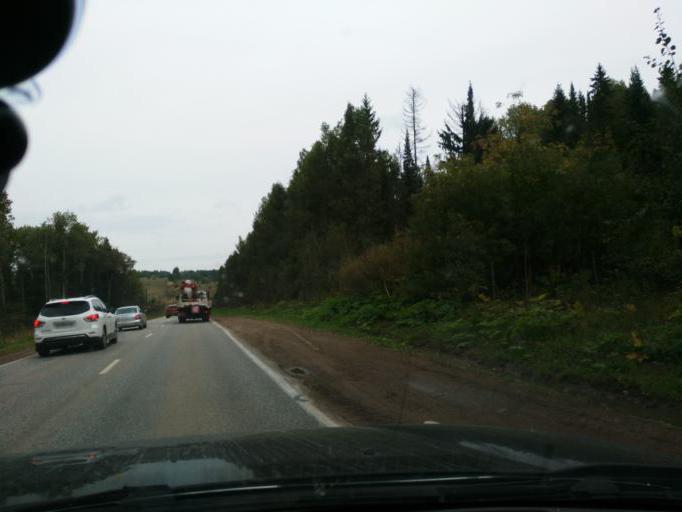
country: RU
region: Perm
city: Chernushka
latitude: 56.5703
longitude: 56.1253
